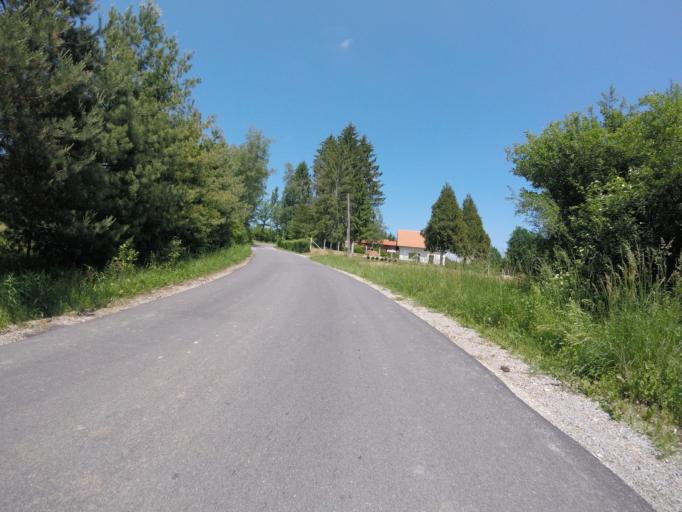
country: HR
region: Grad Zagreb
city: Strmec
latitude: 45.5699
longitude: 15.9474
